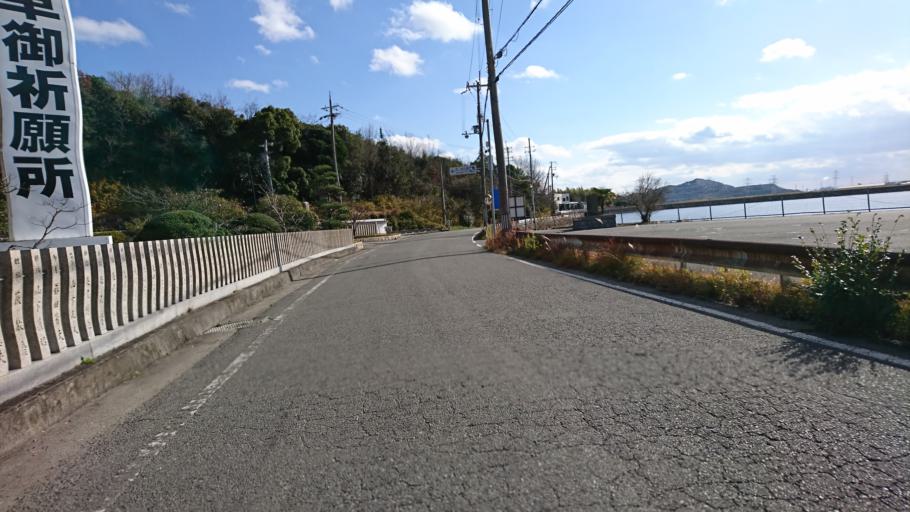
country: JP
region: Hyogo
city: Kakogawacho-honmachi
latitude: 34.8057
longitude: 134.7798
